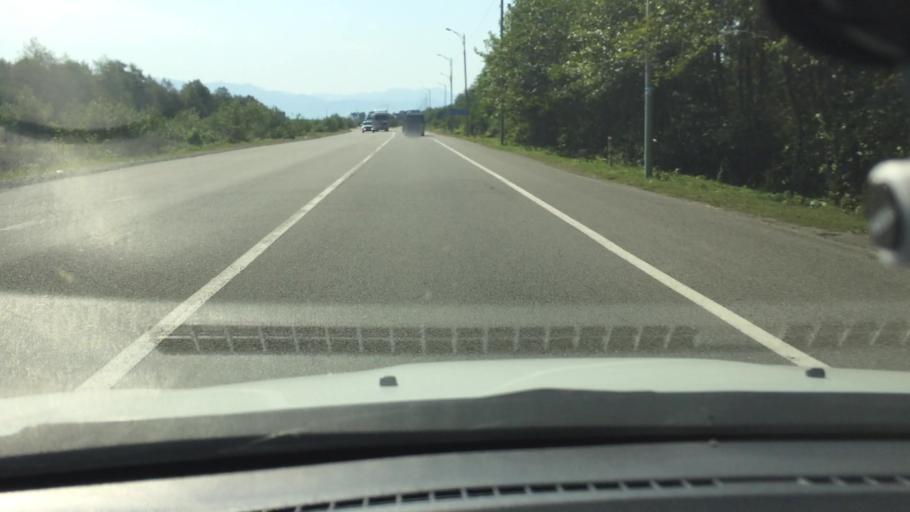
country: GE
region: Guria
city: Urek'i
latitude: 41.9263
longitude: 41.7732
